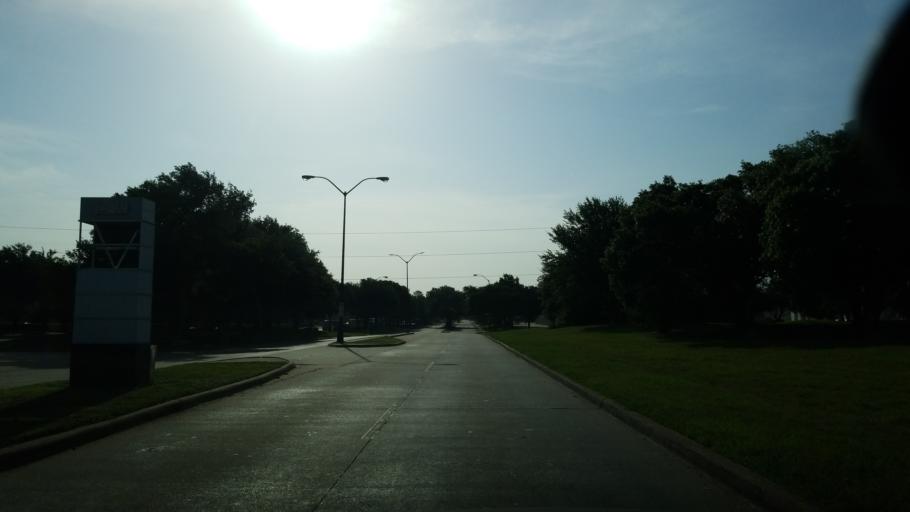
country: US
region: Texas
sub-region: Dallas County
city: Coppell
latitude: 32.9305
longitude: -97.0215
